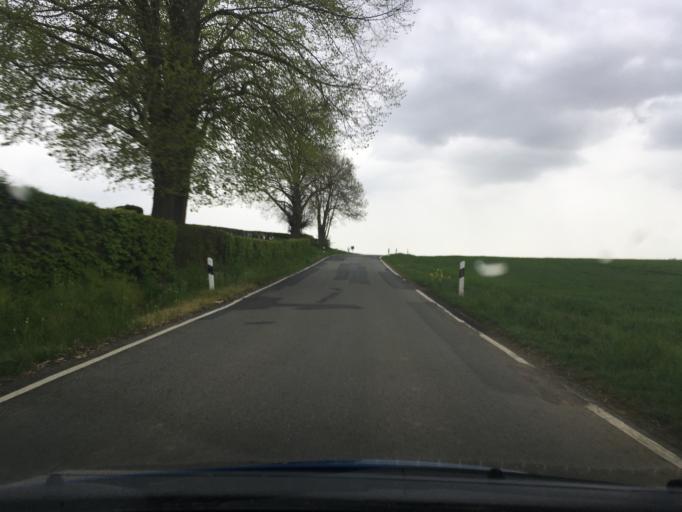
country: DE
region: Lower Saxony
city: Eimen
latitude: 51.8496
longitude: 9.8128
